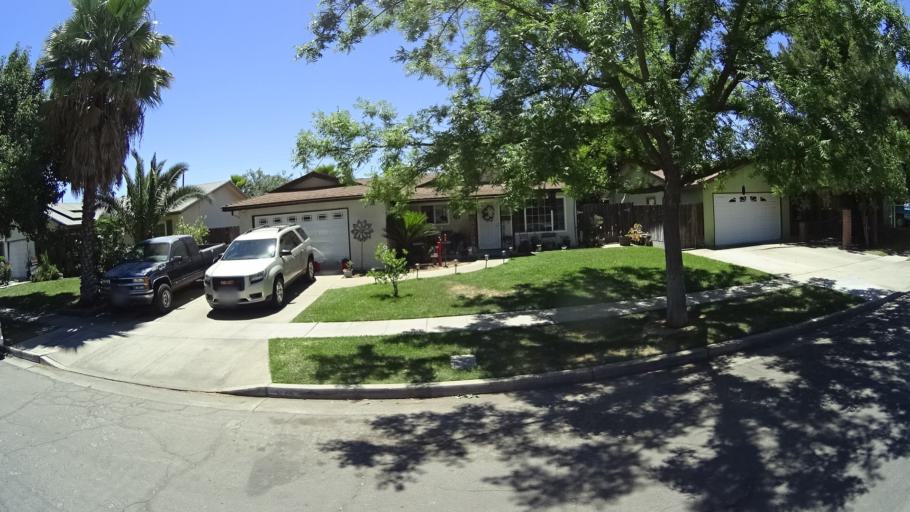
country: US
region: California
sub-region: Fresno County
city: West Park
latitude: 36.7923
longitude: -119.8470
